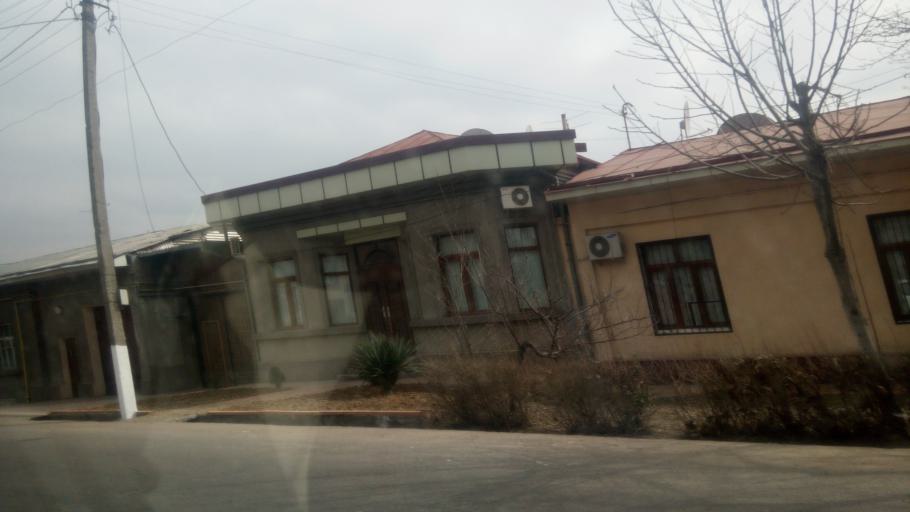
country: UZ
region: Toshkent
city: Salor
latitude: 41.3323
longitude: 69.2957
